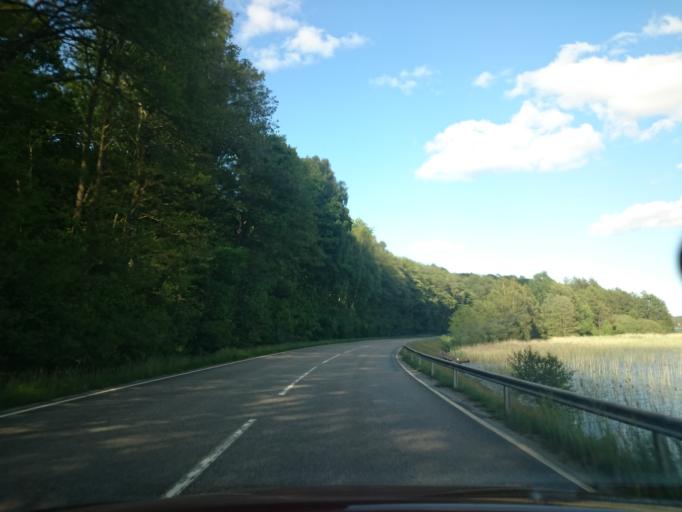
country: SE
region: Vaestra Goetaland
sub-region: Harryda Kommun
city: Landvetter
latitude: 57.6794
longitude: 12.1743
